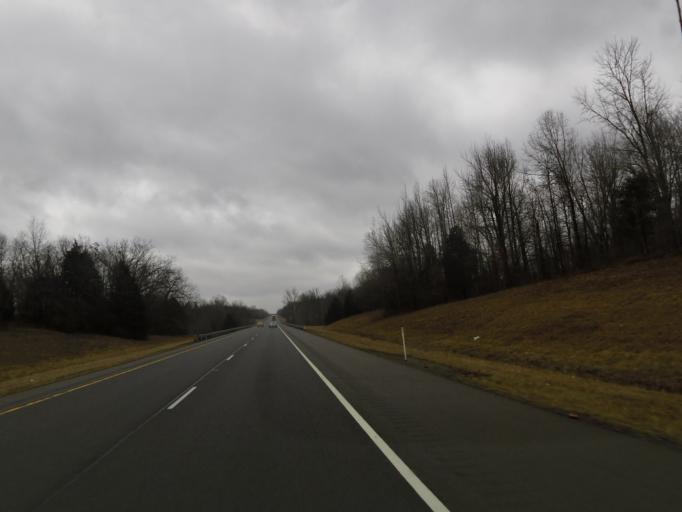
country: US
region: Illinois
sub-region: Johnson County
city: Vienna
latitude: 37.3705
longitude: -88.8088
